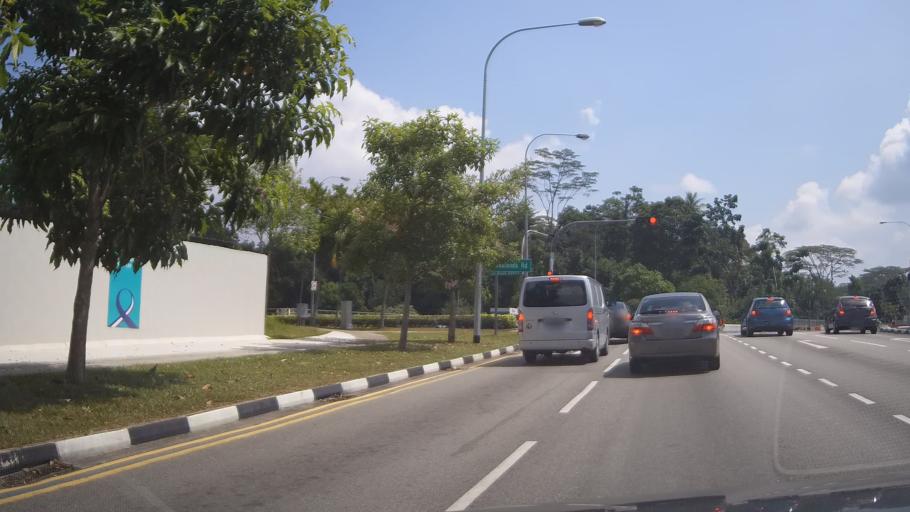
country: SG
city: Singapore
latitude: 1.3414
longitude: 103.7773
